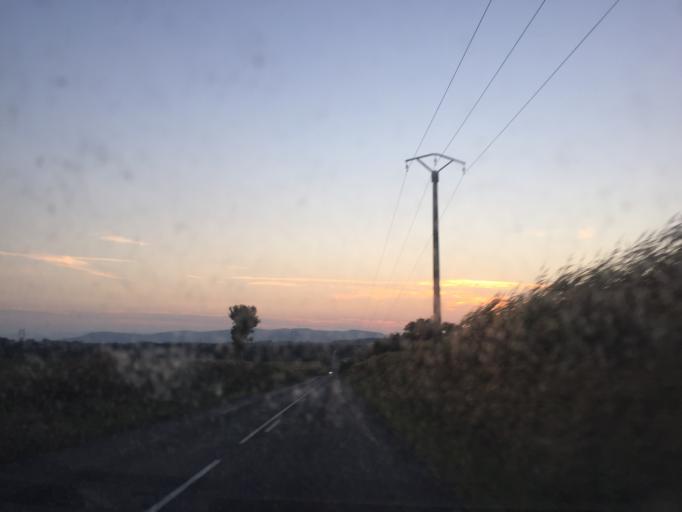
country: FR
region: Rhone-Alpes
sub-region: Departement de l'Ain
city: Tramoyes
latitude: 45.8736
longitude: 4.9456
